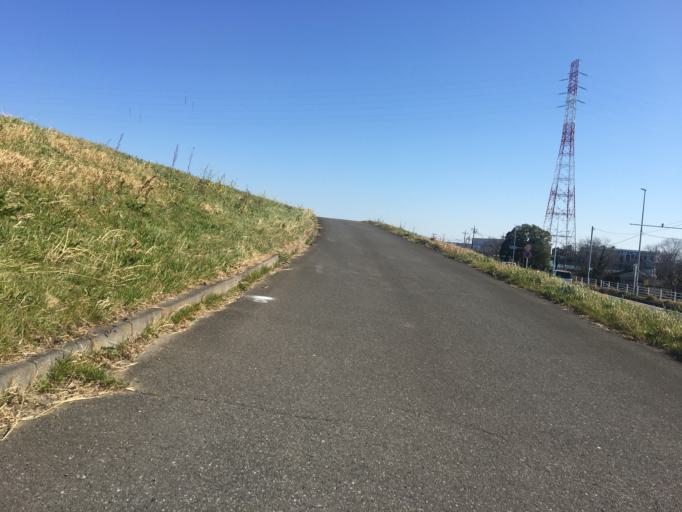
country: JP
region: Saitama
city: Shiki
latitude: 35.8335
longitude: 139.6045
